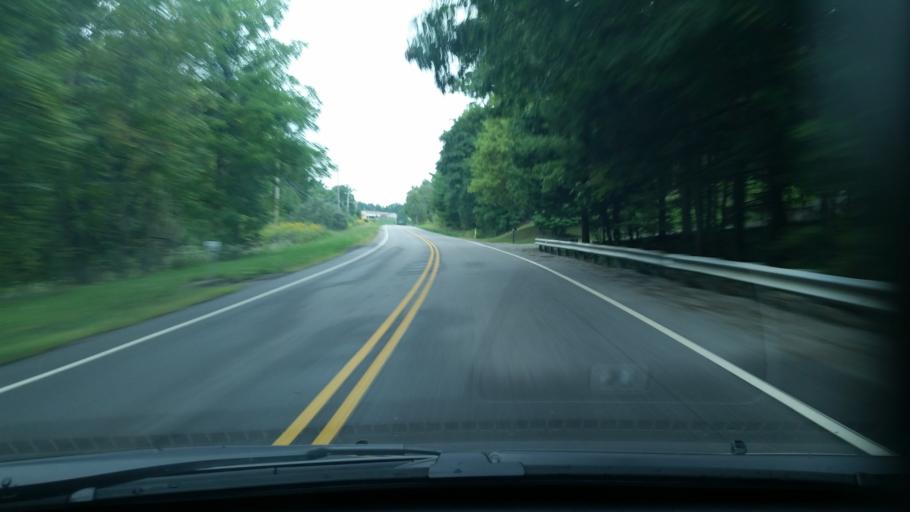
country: US
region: Pennsylvania
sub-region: Clearfield County
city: Shiloh
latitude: 41.0771
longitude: -78.3458
